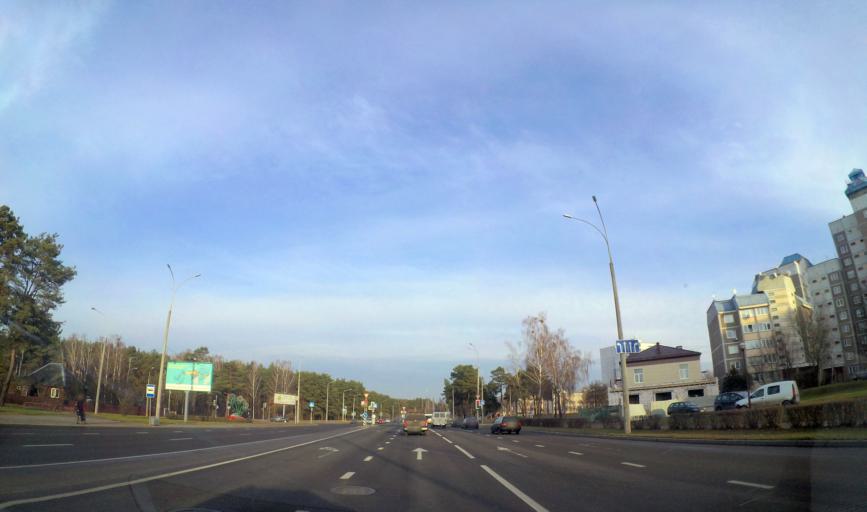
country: BY
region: Grodnenskaya
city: Hrodna
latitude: 53.6723
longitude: 23.7934
